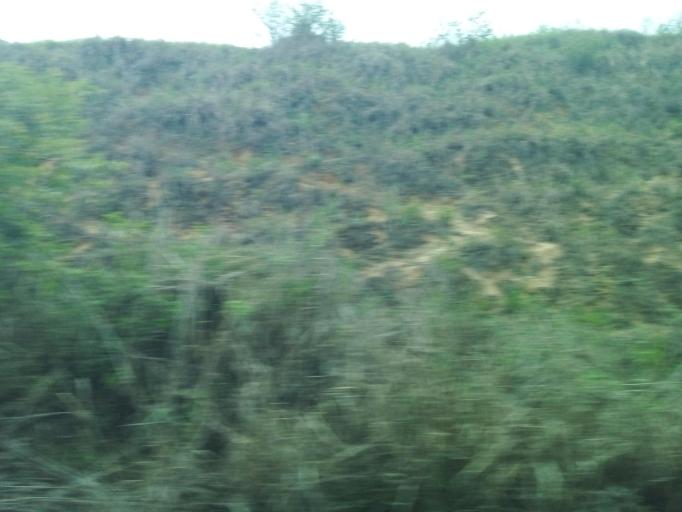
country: BR
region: Minas Gerais
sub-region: Belo Oriente
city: Belo Oriente
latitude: -19.2248
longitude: -42.3002
